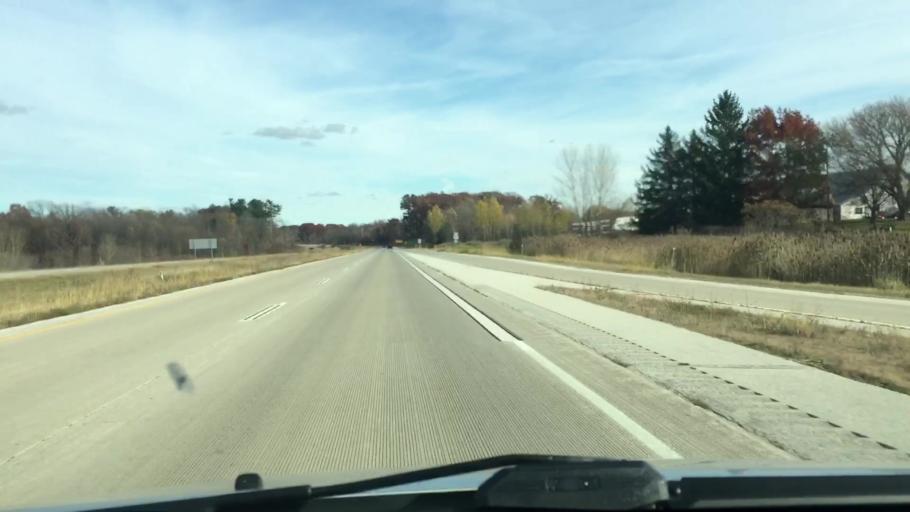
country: US
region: Wisconsin
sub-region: Kewaunee County
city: Luxemburg
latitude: 44.6337
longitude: -87.7717
